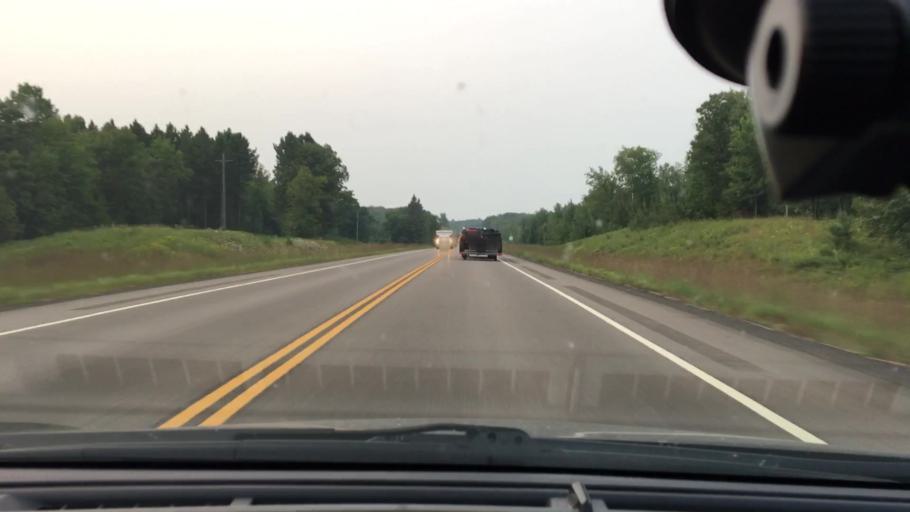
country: US
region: Minnesota
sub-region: Crow Wing County
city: Crosby
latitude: 46.6107
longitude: -93.9490
